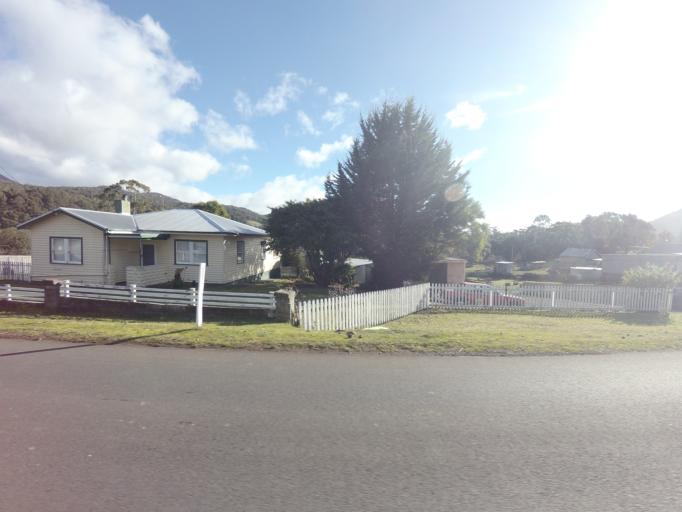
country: AU
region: Tasmania
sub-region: Glenorchy
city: Berriedale
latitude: -42.8422
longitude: 147.1952
